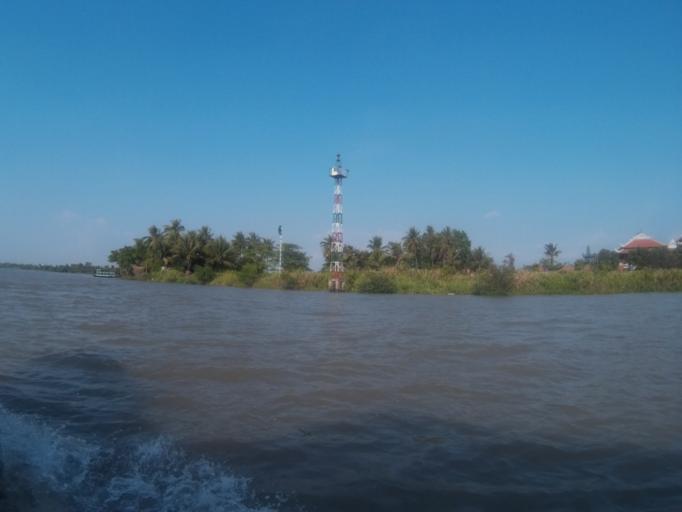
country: VN
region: Dong Nai
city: Bien Hoa
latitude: 10.8794
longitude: 106.8445
